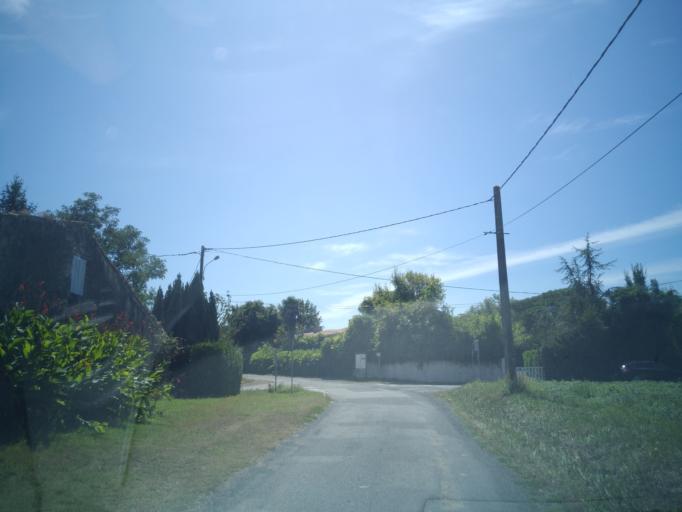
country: FR
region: Poitou-Charentes
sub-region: Departement de la Charente-Maritime
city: Breuillet
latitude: 45.6941
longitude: -1.0743
